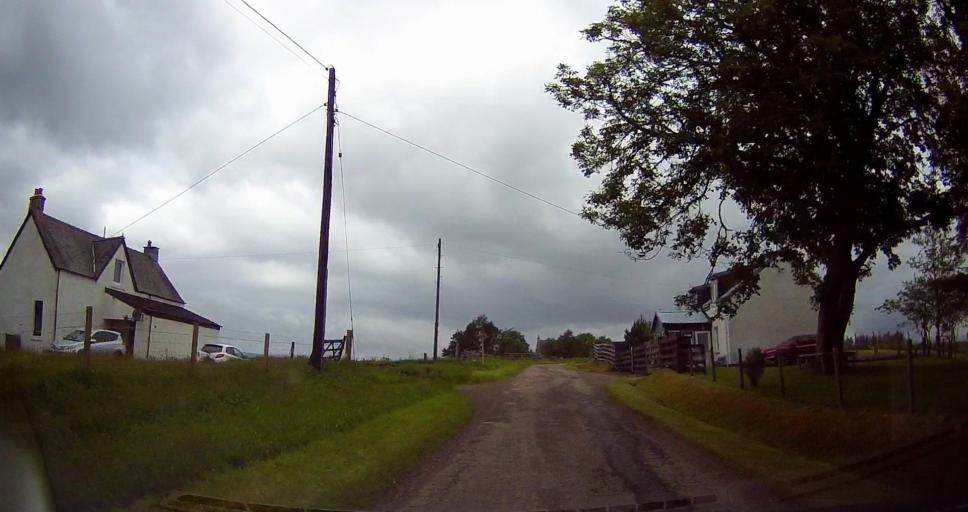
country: GB
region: Scotland
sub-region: Highland
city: Alness
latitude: 58.0718
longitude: -4.4344
